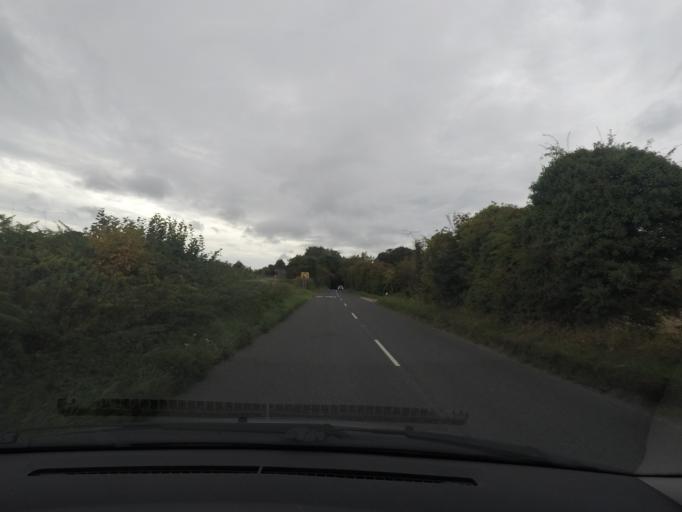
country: GB
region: England
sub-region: Wiltshire
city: Huish
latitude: 51.3788
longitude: -1.7648
